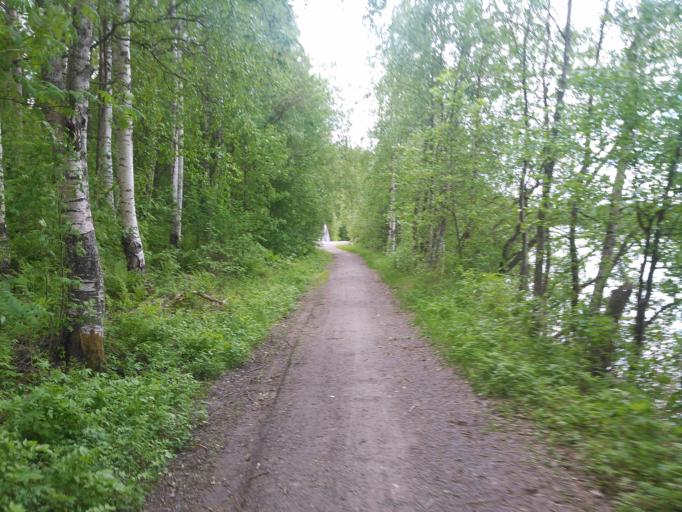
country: SE
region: Vaesterbotten
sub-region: Umea Kommun
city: Roback
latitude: 63.8233
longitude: 20.2139
